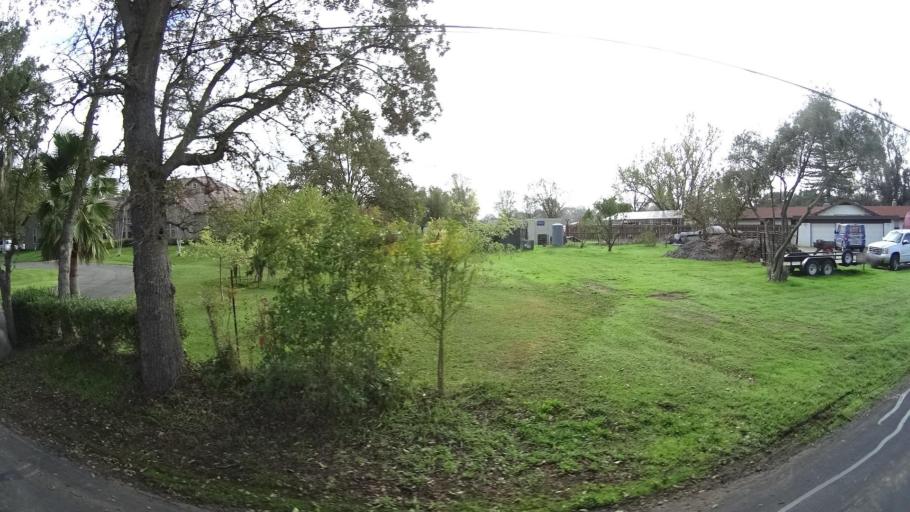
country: US
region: California
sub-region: Sacramento County
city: Vineyard
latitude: 38.4345
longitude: -121.3239
